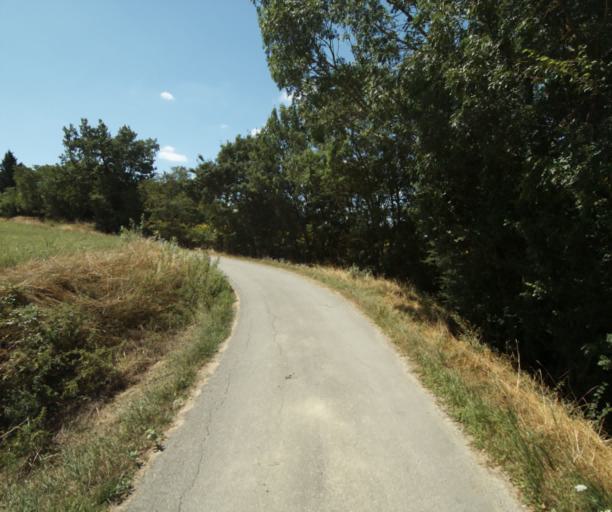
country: FR
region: Midi-Pyrenees
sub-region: Departement de la Haute-Garonne
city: Saint-Felix-Lauragais
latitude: 43.4786
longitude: 1.8617
